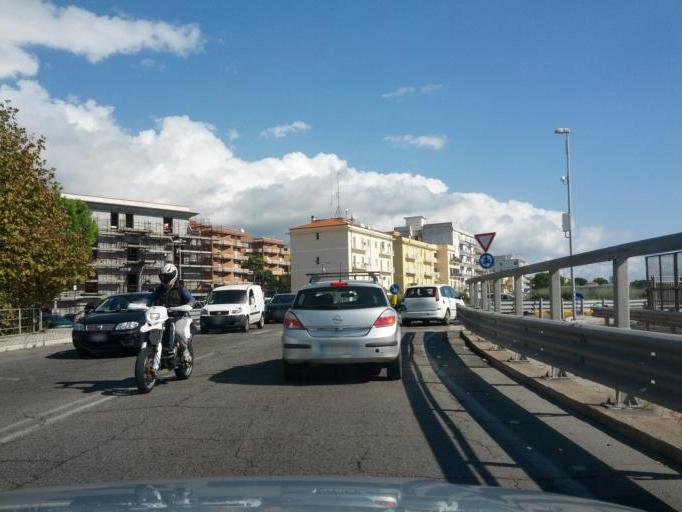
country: IT
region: Latium
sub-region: Provincia di Latina
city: Formia
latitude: 41.2604
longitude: 13.6186
